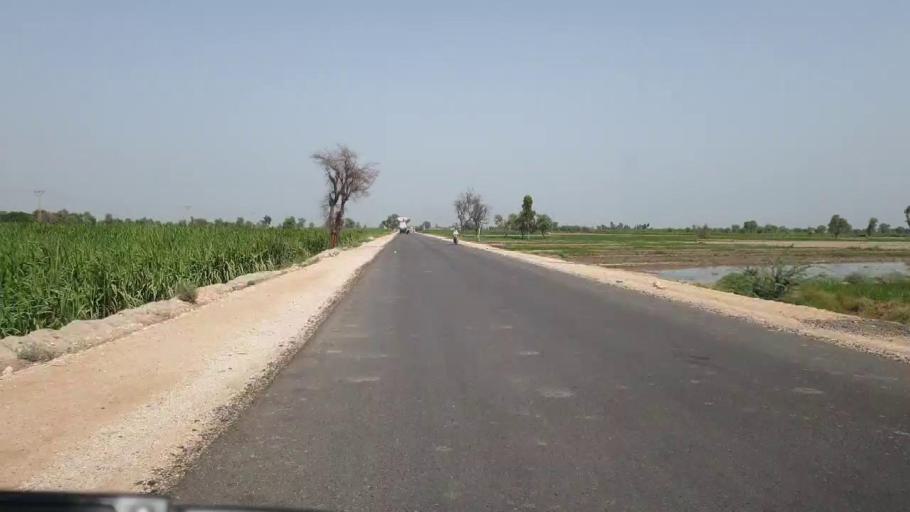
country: PK
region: Sindh
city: Sakrand
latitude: 26.2701
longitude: 68.1633
